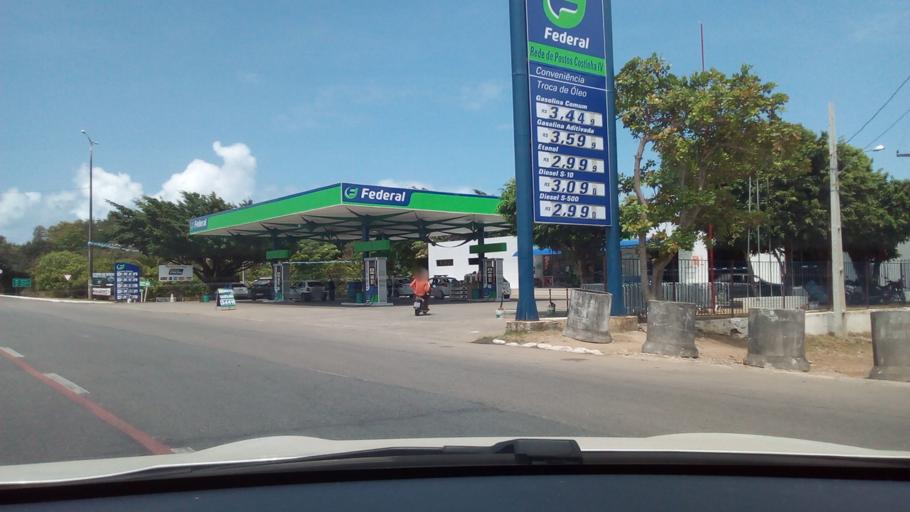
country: BR
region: Paraiba
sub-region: Joao Pessoa
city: Joao Pessoa
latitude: -7.1619
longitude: -34.8006
